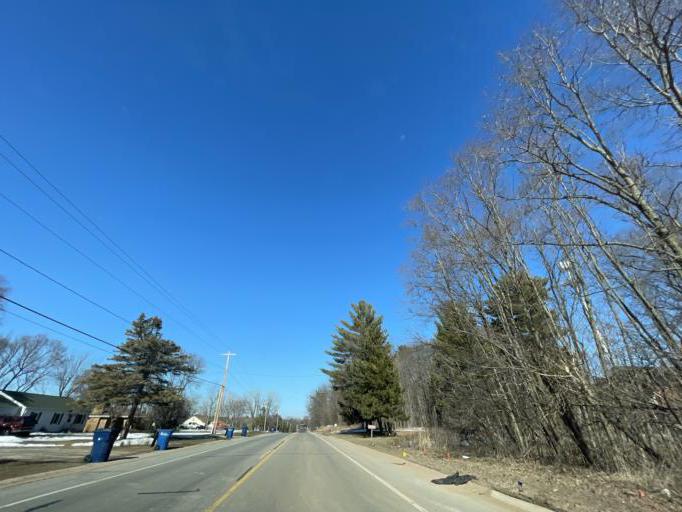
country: US
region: Wisconsin
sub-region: Brown County
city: Suamico
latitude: 44.6132
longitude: -88.0705
